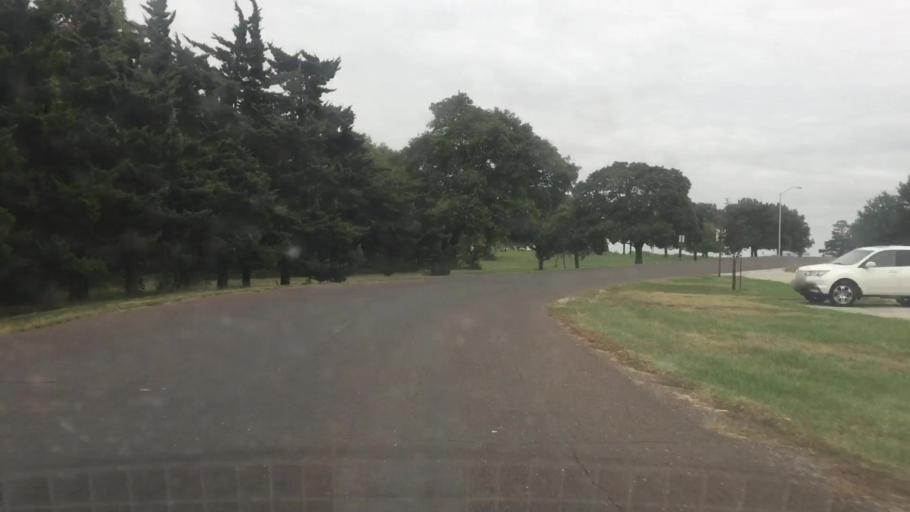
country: US
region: Kansas
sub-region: Johnson County
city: Lenexa
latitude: 38.9863
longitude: -94.7843
